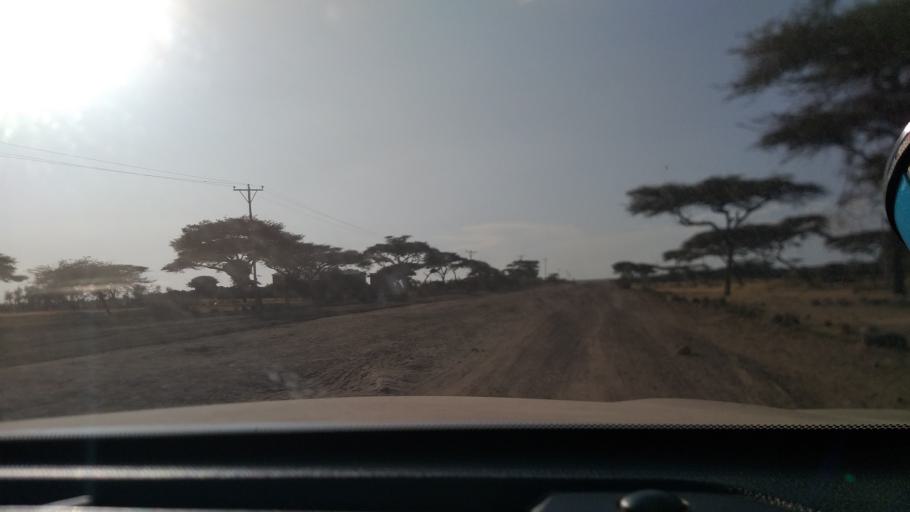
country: ET
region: Oromiya
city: Shashemene
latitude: 7.4973
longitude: 38.7013
